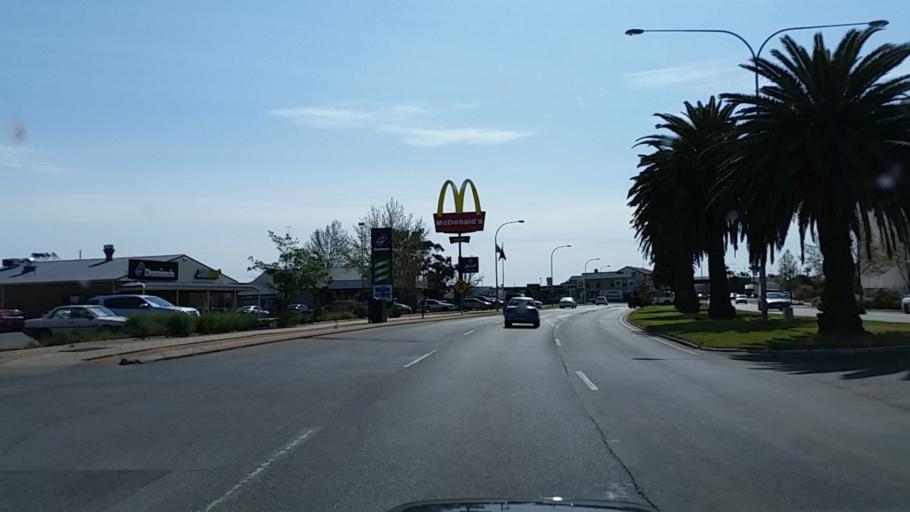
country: AU
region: South Australia
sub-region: Port Pirie City and Dists
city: Port Pirie
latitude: -33.1813
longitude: 138.0132
